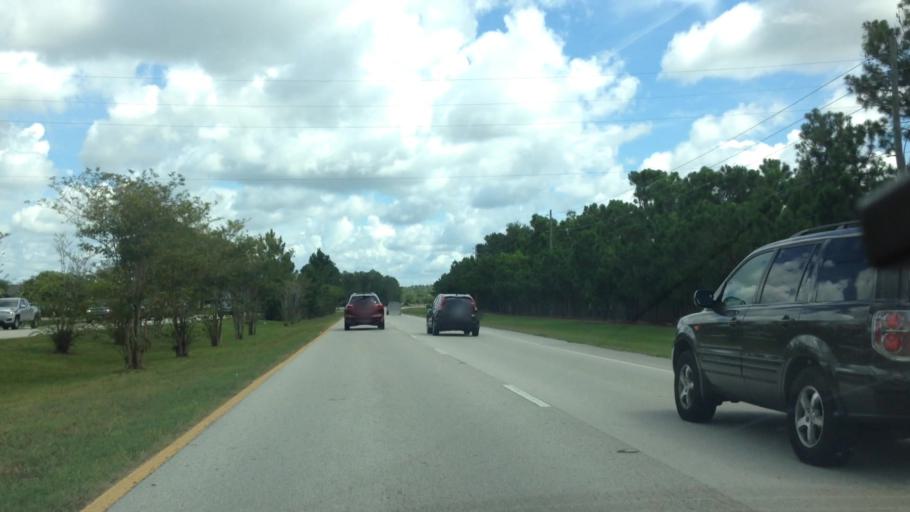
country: US
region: Florida
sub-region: Duval County
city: Jacksonville Beach
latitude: 30.2580
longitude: -81.4665
